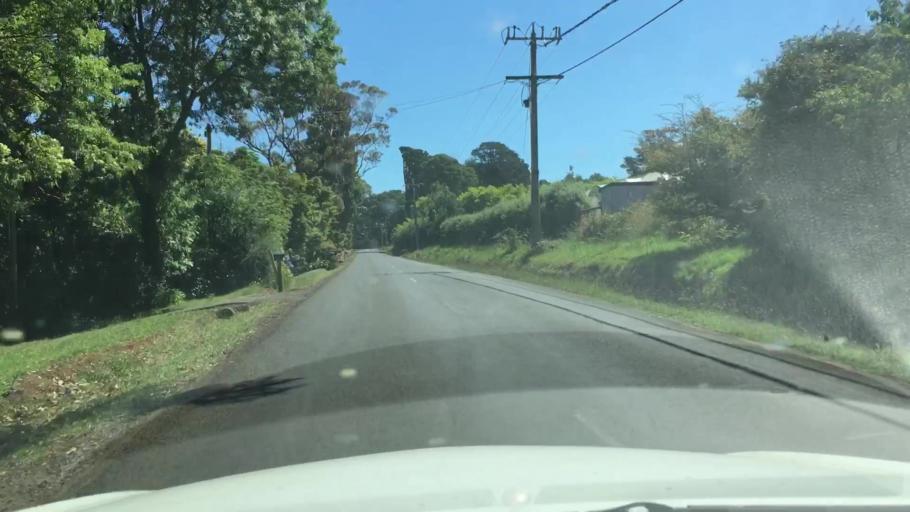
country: AU
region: Victoria
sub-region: Yarra Ranges
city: Mount Evelyn
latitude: -37.8112
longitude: 145.4269
